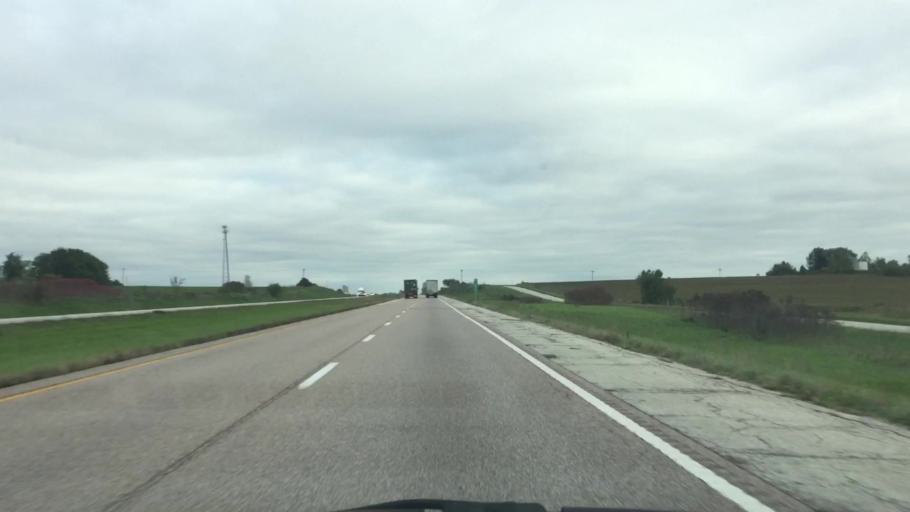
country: US
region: Missouri
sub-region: Clinton County
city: Lathrop
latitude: 39.5675
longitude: -94.2633
